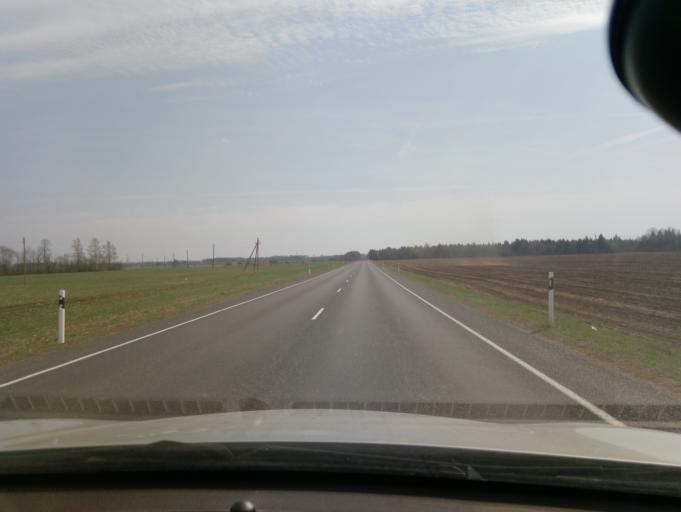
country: EE
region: Viljandimaa
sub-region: Vohma linn
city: Vohma
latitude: 58.7510
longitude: 25.5674
